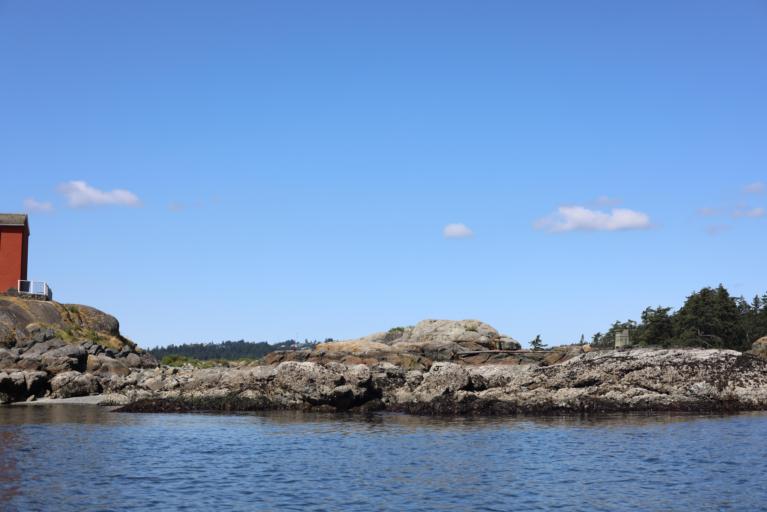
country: CA
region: British Columbia
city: Colwood
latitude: 48.4309
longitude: -123.4464
